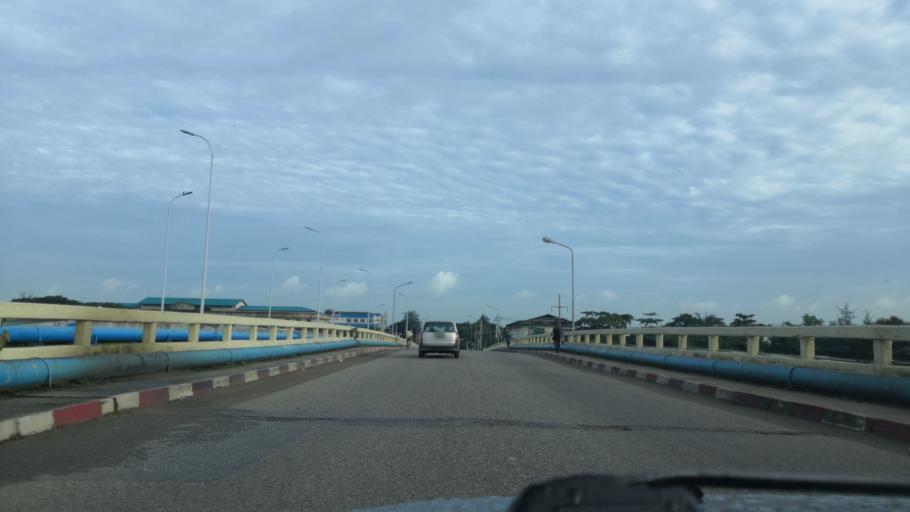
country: MM
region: Yangon
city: Yangon
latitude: 16.8892
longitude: 96.1617
